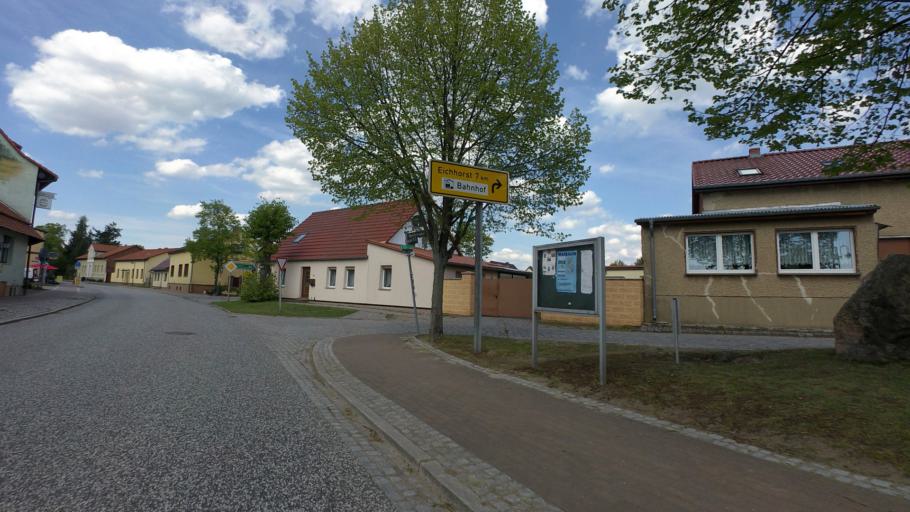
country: DE
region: Brandenburg
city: Marienwerder
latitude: 52.9049
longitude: 13.5340
